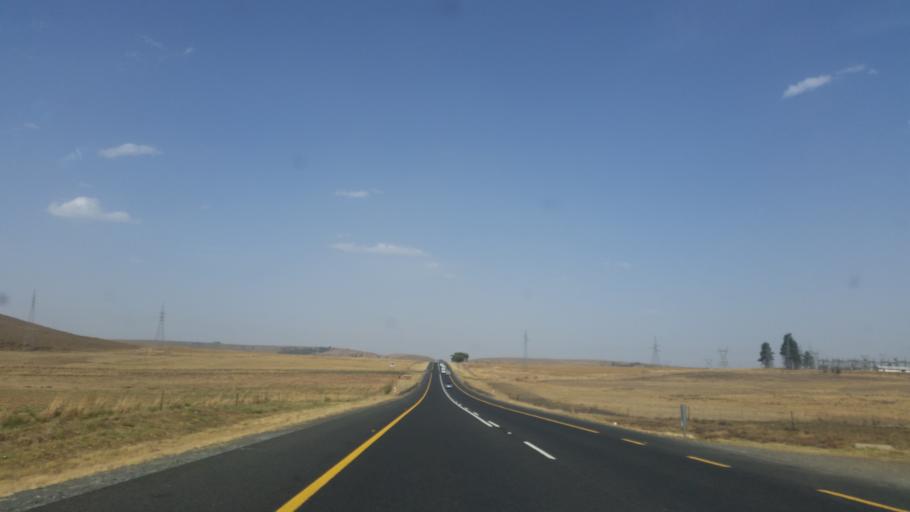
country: ZA
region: Orange Free State
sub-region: Thabo Mofutsanyana District Municipality
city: Phuthaditjhaba
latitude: -28.2826
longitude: 28.6418
